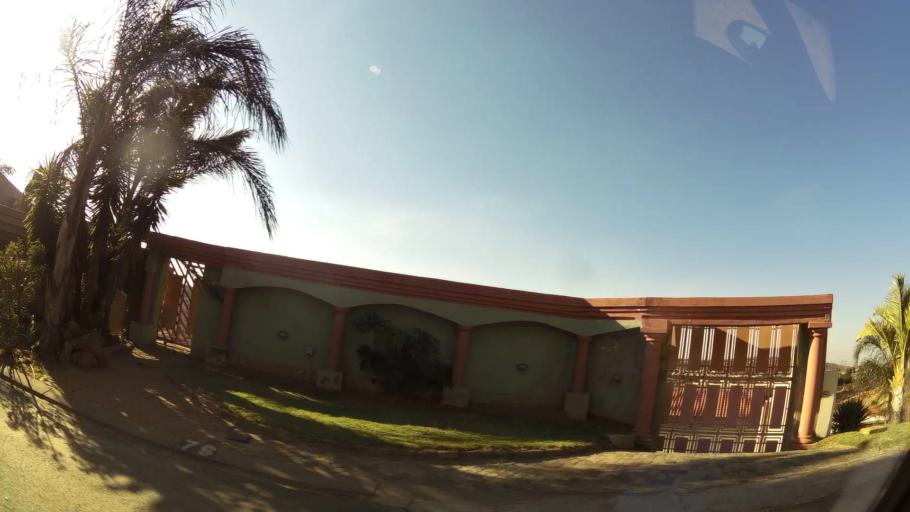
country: ZA
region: Gauteng
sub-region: City of Johannesburg Metropolitan Municipality
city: Johannesburg
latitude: -26.2702
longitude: 28.0572
